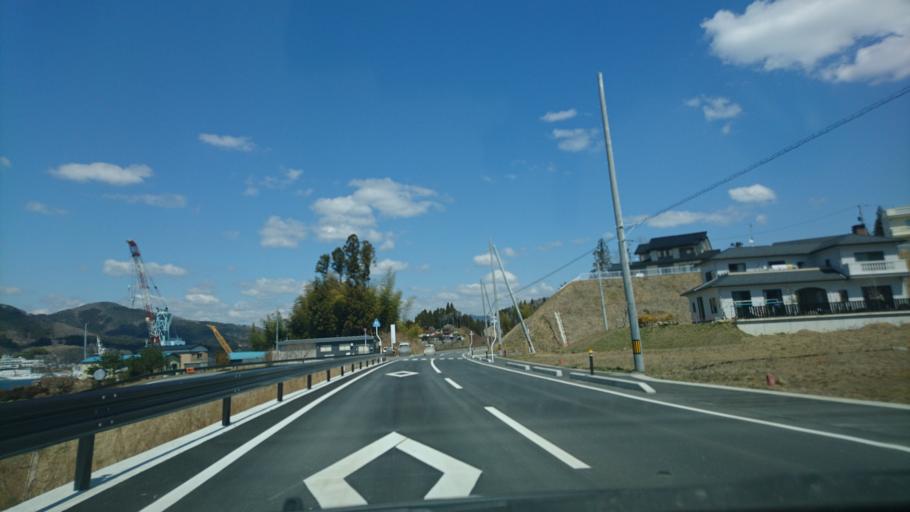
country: JP
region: Iwate
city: Ofunato
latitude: 38.8999
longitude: 141.5895
